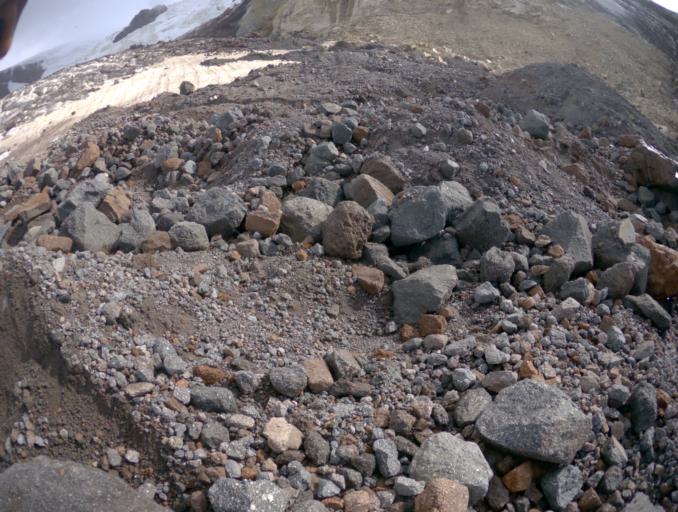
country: RU
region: Kabardino-Balkariya
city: Terskol
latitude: 43.3845
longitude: 42.4190
